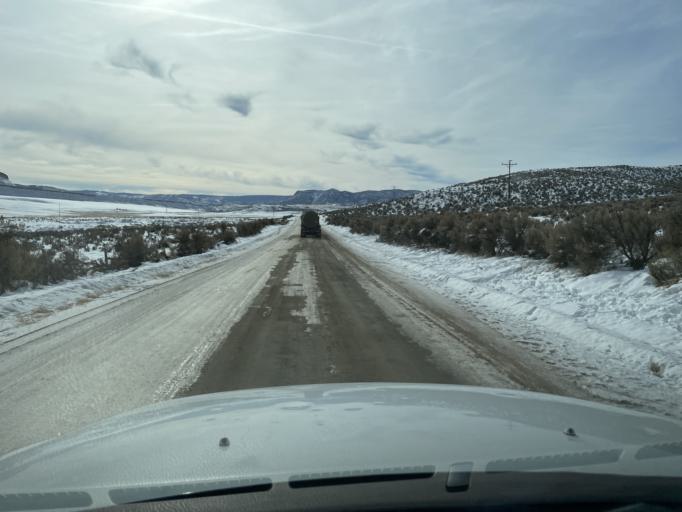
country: US
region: Colorado
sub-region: Moffat County
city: Craig
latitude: 40.3303
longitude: -107.6871
